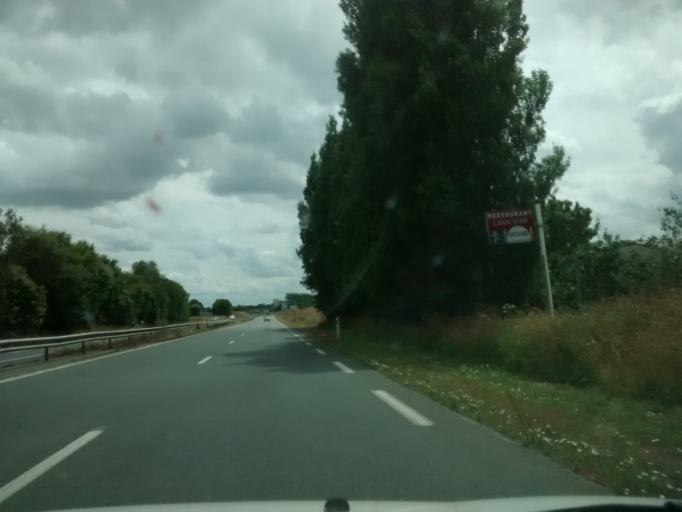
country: FR
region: Brittany
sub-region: Departement des Cotes-d'Armor
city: Cavan
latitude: 48.6504
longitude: -3.3301
